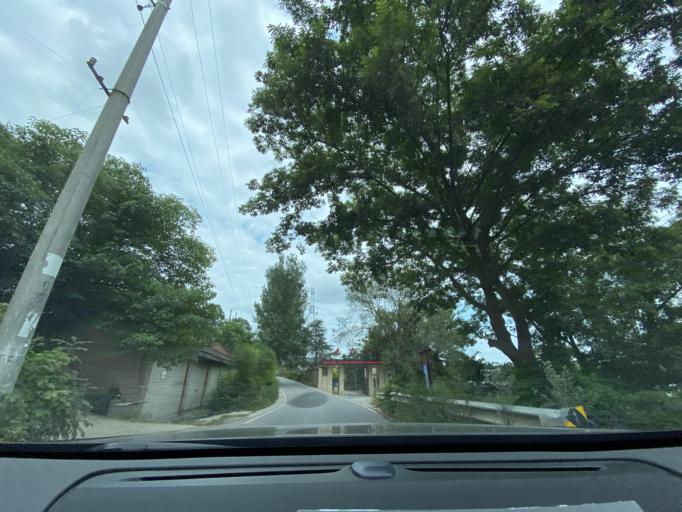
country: CN
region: Sichuan
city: Jiancheng
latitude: 30.4381
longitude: 104.5345
